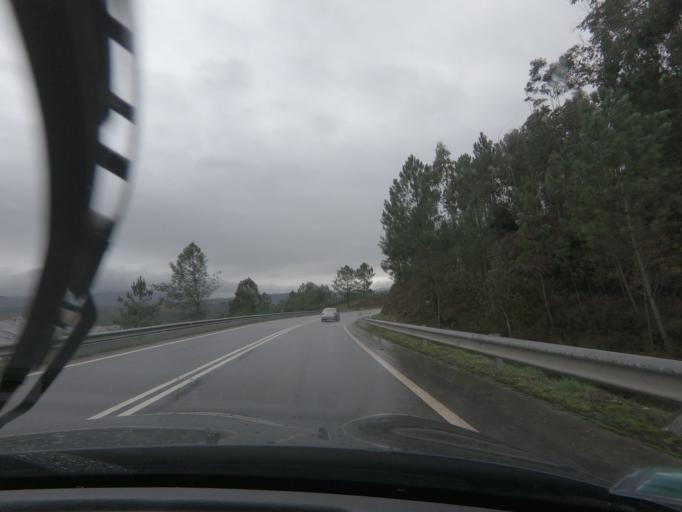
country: PT
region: Braga
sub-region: Celorico de Basto
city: Celorico de Basto
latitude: 41.3320
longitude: -8.0383
